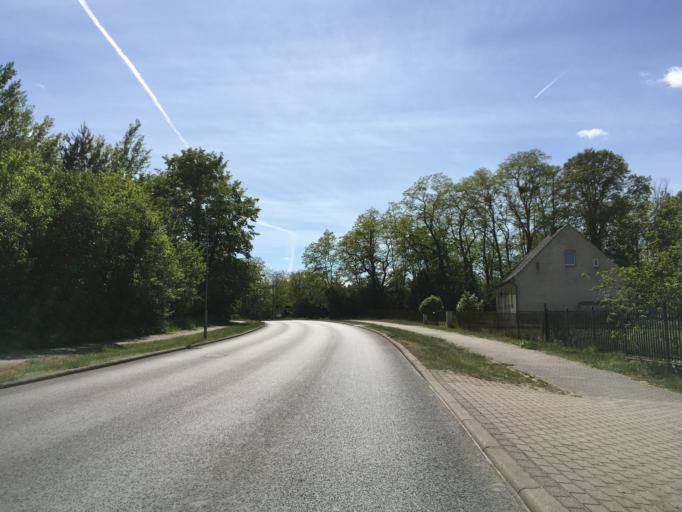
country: DE
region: Brandenburg
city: Oderberg
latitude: 52.8323
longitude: 14.0776
